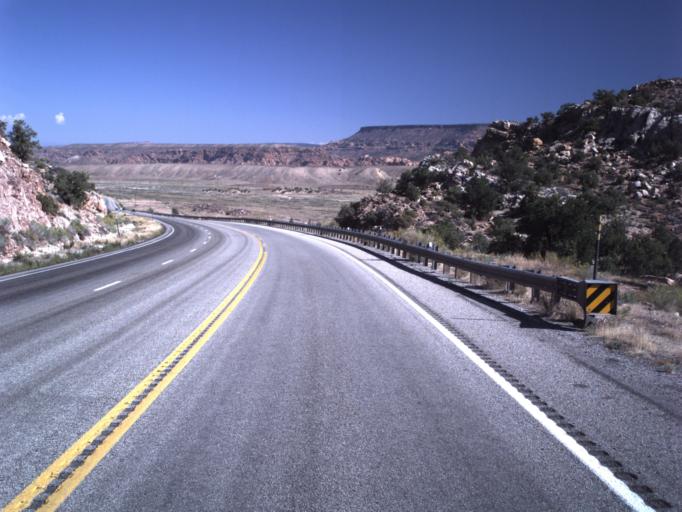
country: US
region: Utah
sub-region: Grand County
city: Moab
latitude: 38.4264
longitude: -109.4276
